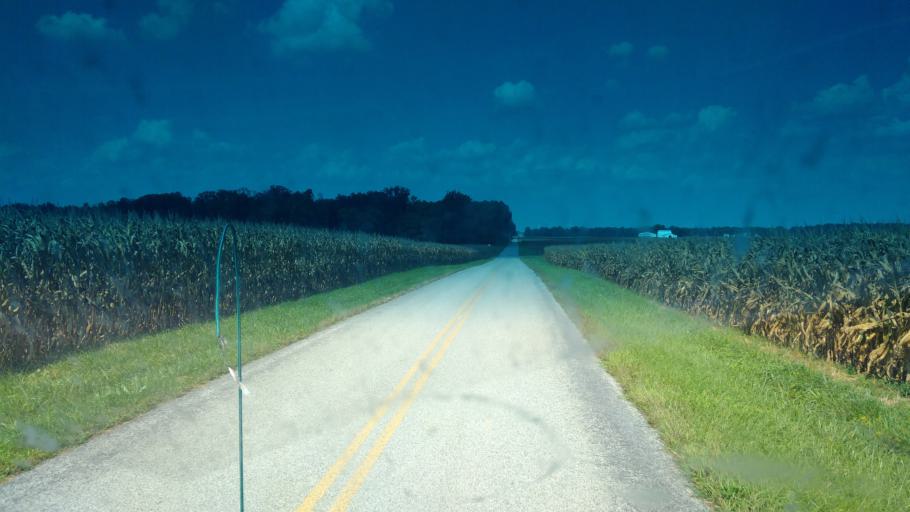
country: US
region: Ohio
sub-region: Hardin County
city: Ada
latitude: 40.7213
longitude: -83.7660
